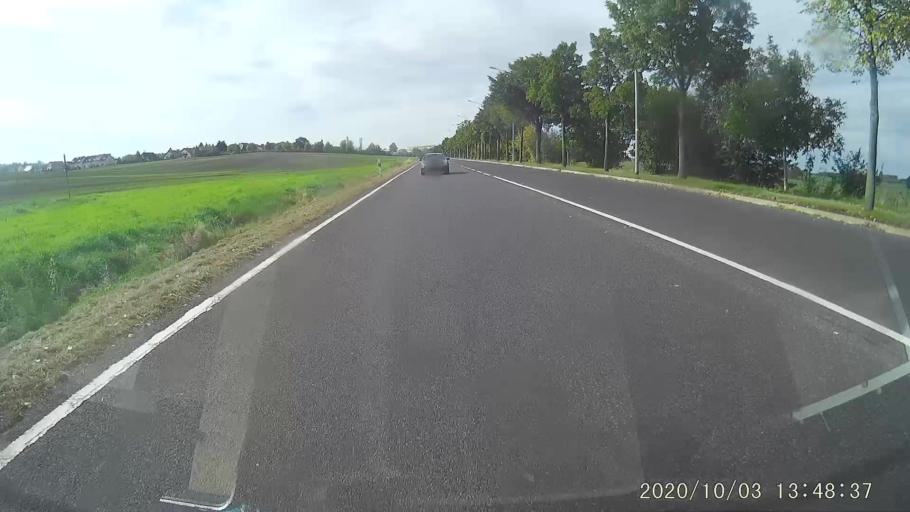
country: DE
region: Saxony
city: Goerlitz
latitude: 51.1705
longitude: 14.9934
